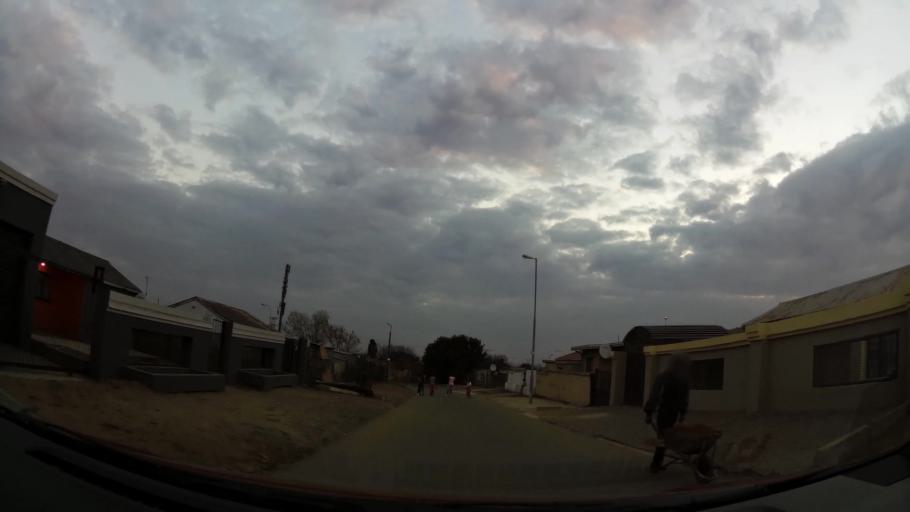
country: ZA
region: Gauteng
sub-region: City of Johannesburg Metropolitan Municipality
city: Soweto
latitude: -26.2484
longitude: 27.9238
